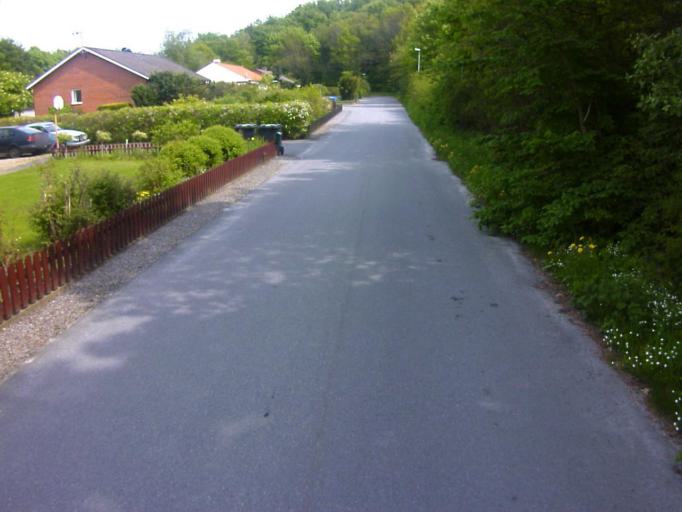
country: SE
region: Blekinge
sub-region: Karlshamns Kommun
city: Morrum
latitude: 56.0380
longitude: 14.7587
